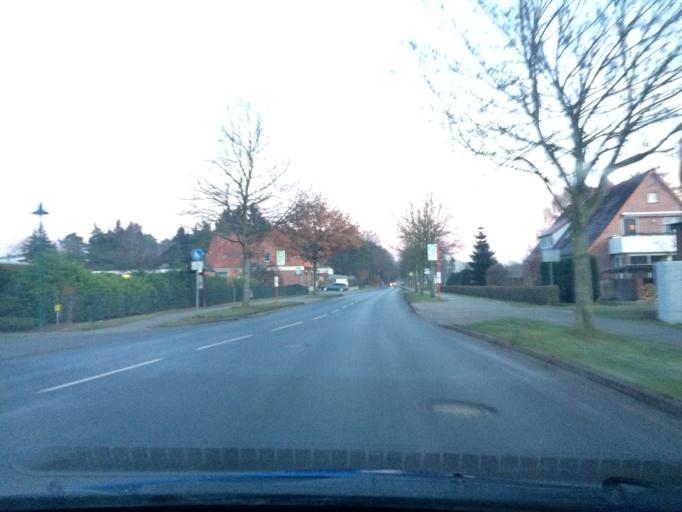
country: DE
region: Lower Saxony
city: Embsen
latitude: 53.1807
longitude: 10.3605
